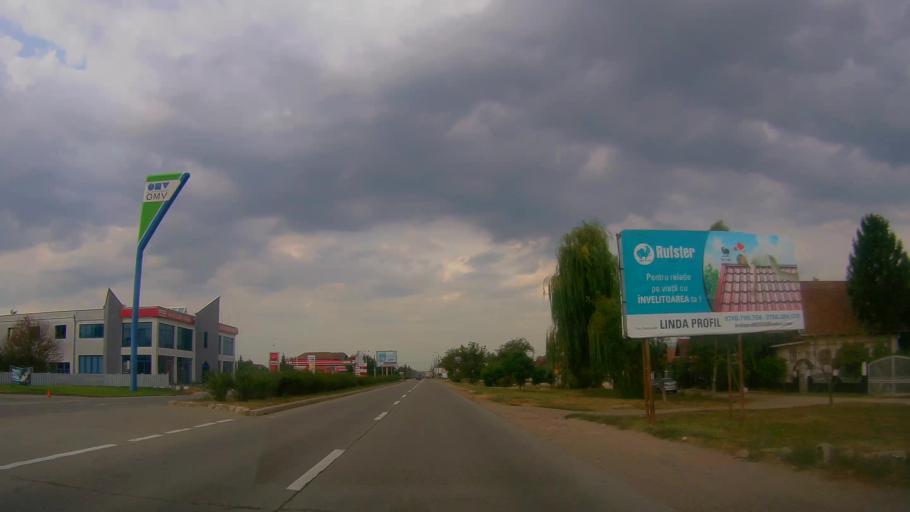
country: RO
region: Satu Mare
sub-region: Comuna Paulesti
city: Paulesti
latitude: 47.8078
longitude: 22.9159
